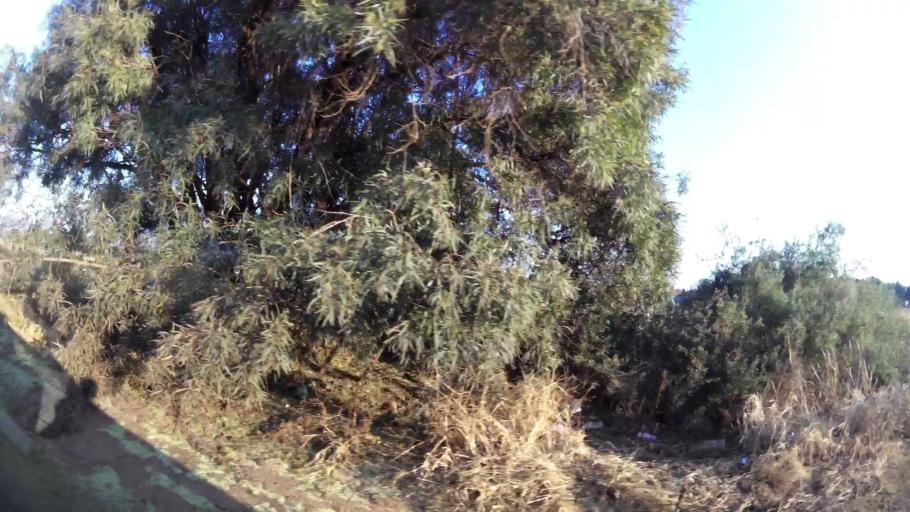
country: ZA
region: Orange Free State
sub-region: Mangaung Metropolitan Municipality
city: Bloemfontein
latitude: -29.0781
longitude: 26.1502
